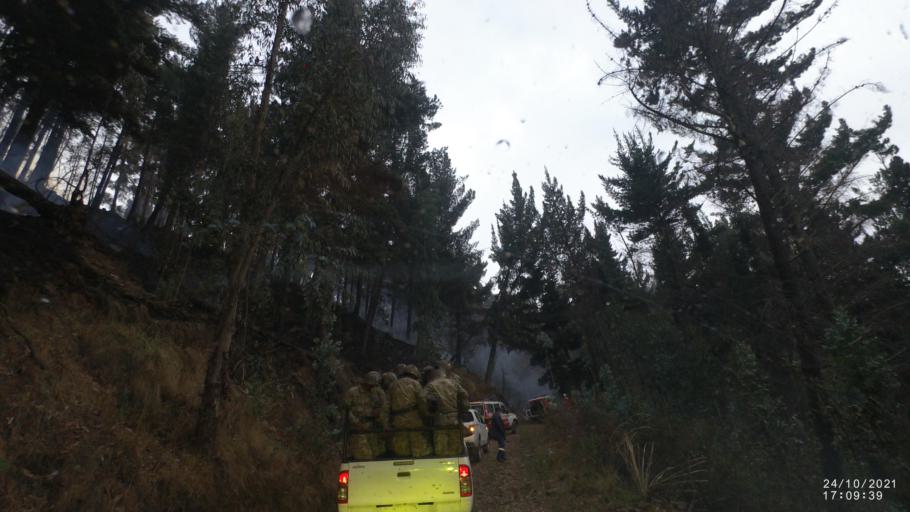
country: BO
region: Cochabamba
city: Cochabamba
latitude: -17.3308
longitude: -66.1378
